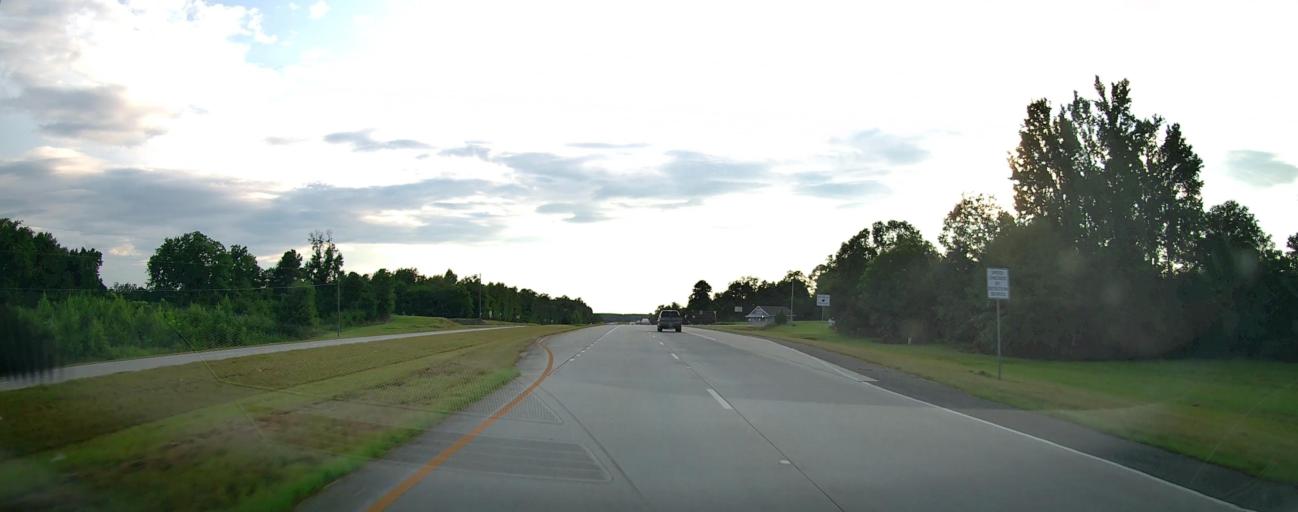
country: US
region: Georgia
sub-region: Peach County
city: Fort Valley
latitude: 32.5556
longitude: -83.9563
